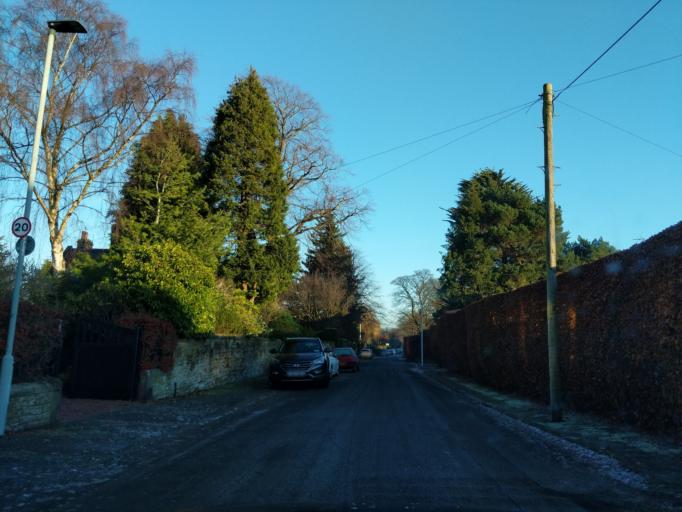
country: GB
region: Scotland
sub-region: Edinburgh
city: Colinton
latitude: 55.9090
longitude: -3.2656
